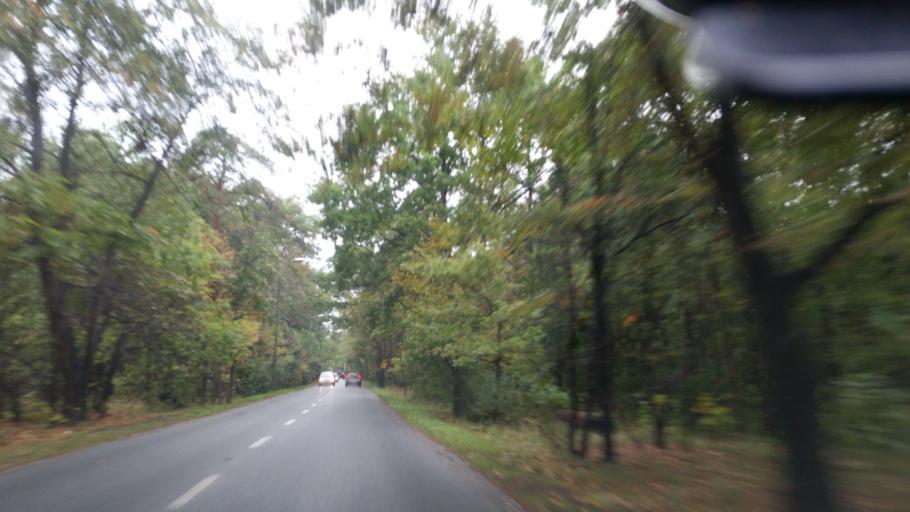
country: PL
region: Masovian Voivodeship
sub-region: Warszawa
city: Bemowo
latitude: 52.2630
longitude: 20.8887
